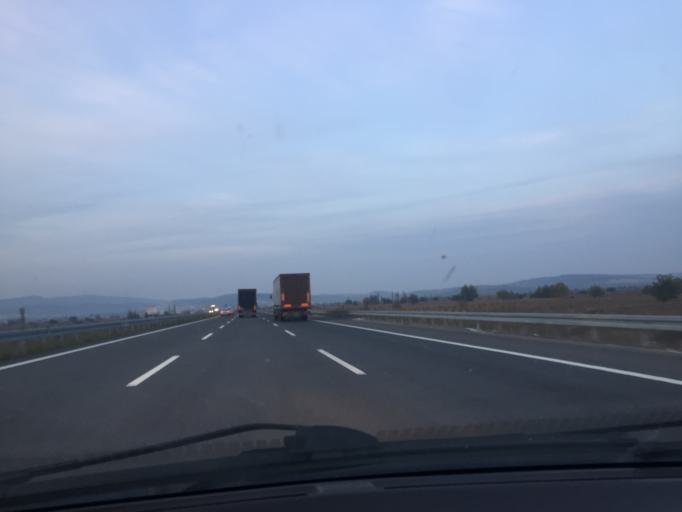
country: TR
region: Manisa
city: Halitpasa
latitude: 38.7484
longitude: 27.6597
